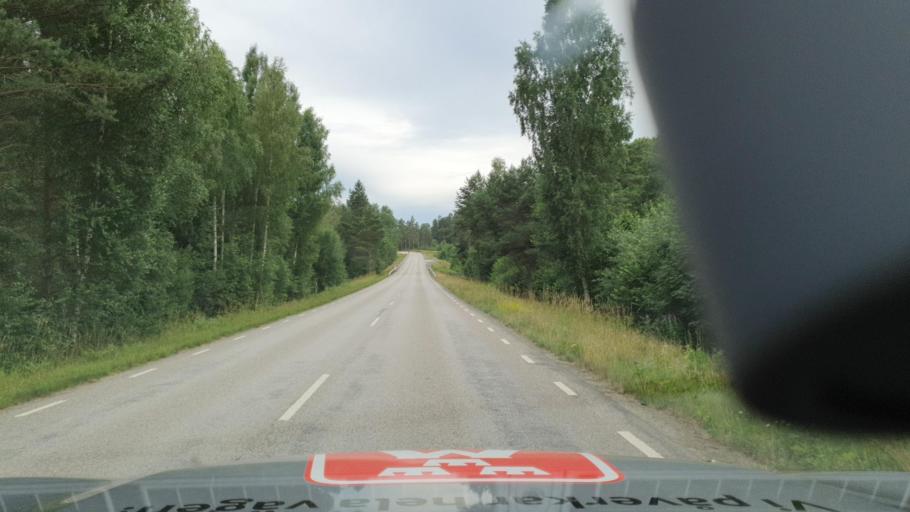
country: SE
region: Kalmar
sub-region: Nybro Kommun
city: Nybro
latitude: 56.7148
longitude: 15.9695
